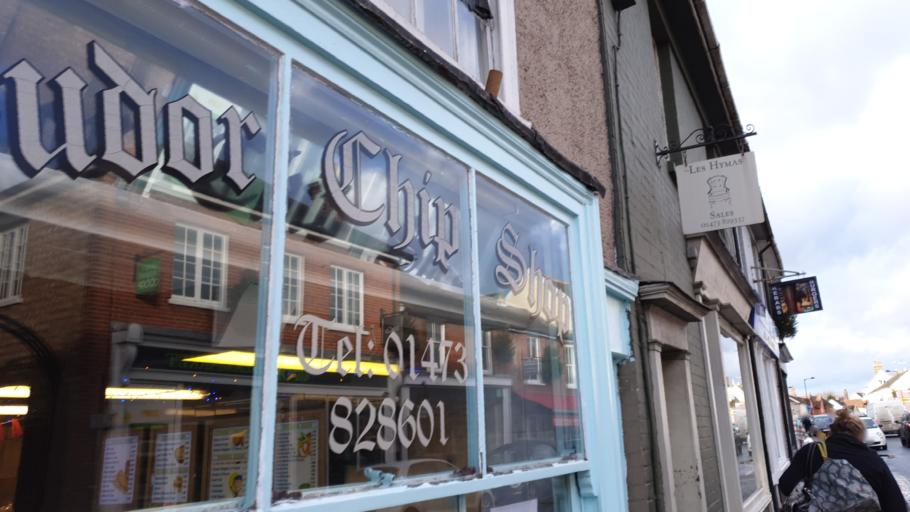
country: GB
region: England
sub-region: Suffolk
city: Hadleigh
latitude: 52.0441
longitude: 0.9536
